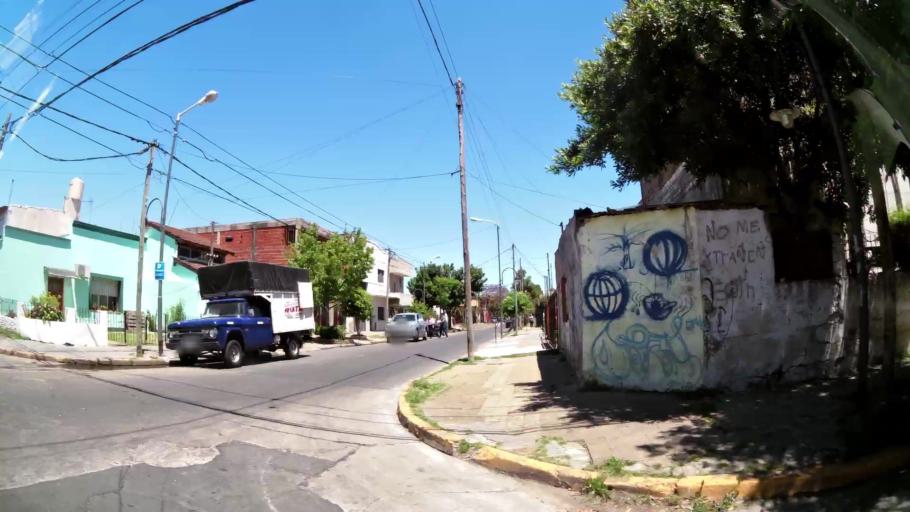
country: AR
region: Buenos Aires
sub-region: Partido de Tigre
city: Tigre
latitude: -34.4548
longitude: -58.5547
